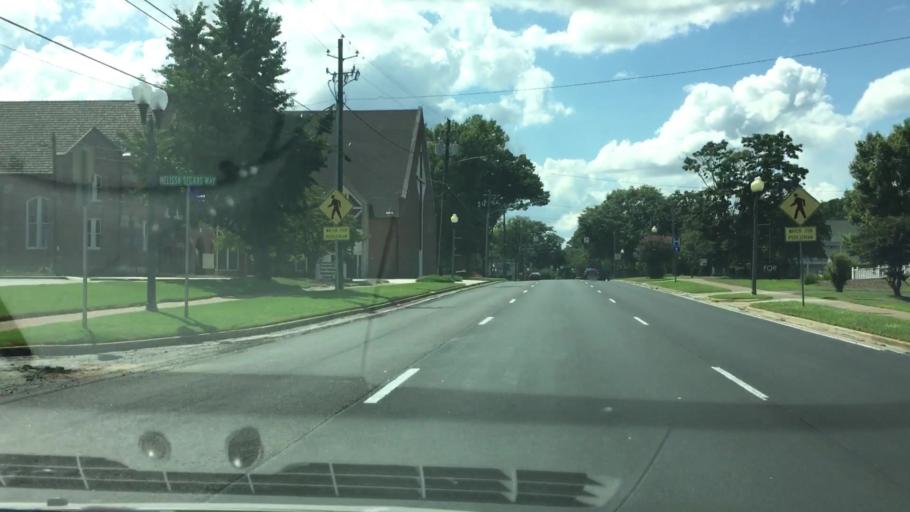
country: US
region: Georgia
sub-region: Fayette County
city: Fayetteville
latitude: 33.4487
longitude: -84.4526
